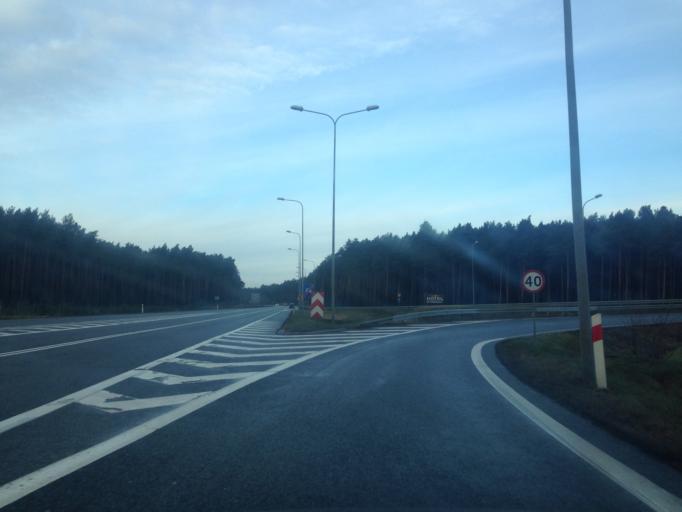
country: PL
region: Kujawsko-Pomorskie
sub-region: Powiat torunski
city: Wielka Nieszawka
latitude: 52.9715
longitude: 18.5393
